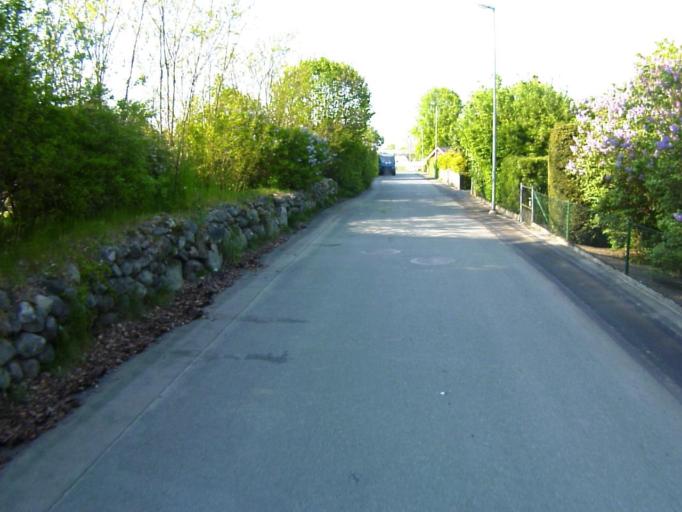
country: SE
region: Skane
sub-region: Kristianstads Kommun
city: Onnestad
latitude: 56.0593
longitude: 14.0277
